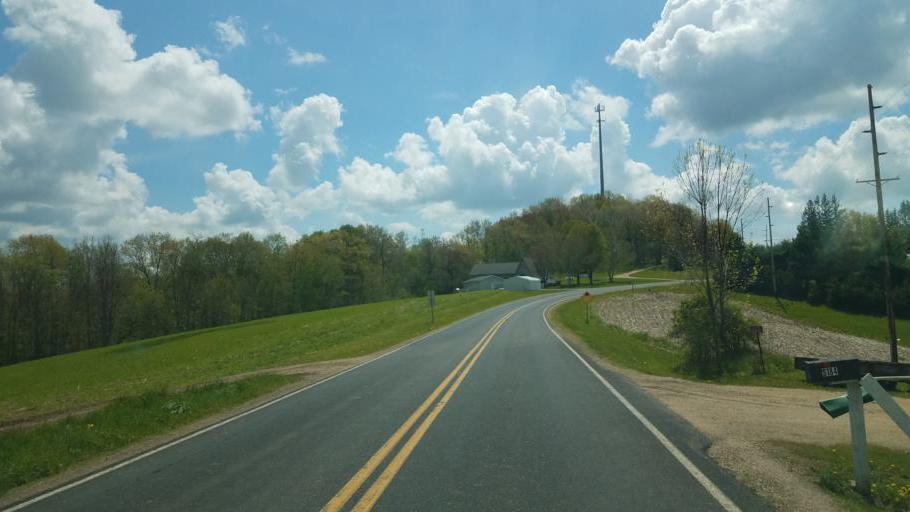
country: US
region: Wisconsin
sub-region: Vernon County
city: Hillsboro
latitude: 43.6647
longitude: -90.3476
